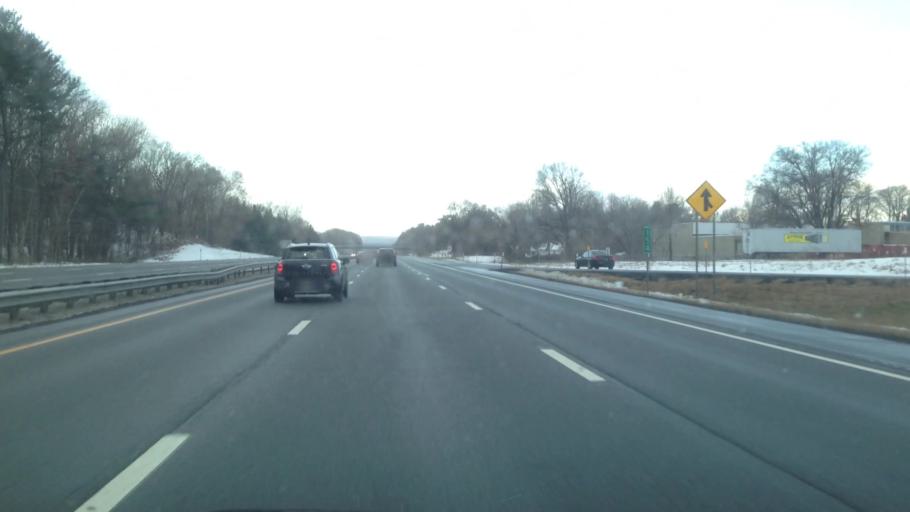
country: US
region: New York
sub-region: Schenectady County
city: Rotterdam
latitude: 42.7554
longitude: -73.9362
